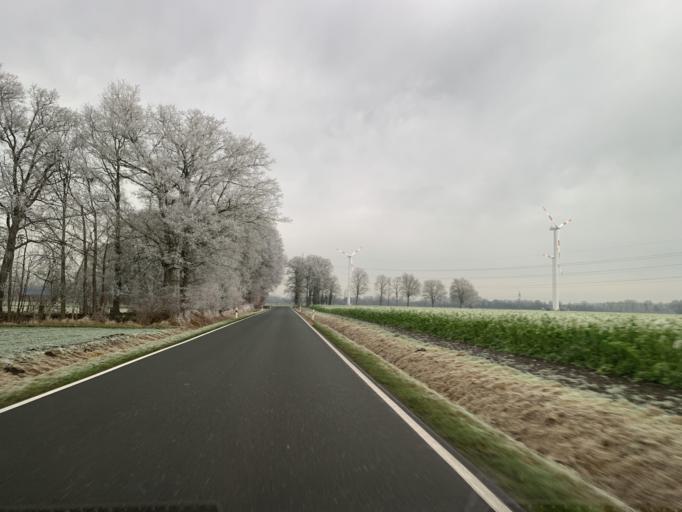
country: DE
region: North Rhine-Westphalia
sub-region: Regierungsbezirk Munster
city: Greven
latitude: 52.0669
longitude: 7.5660
